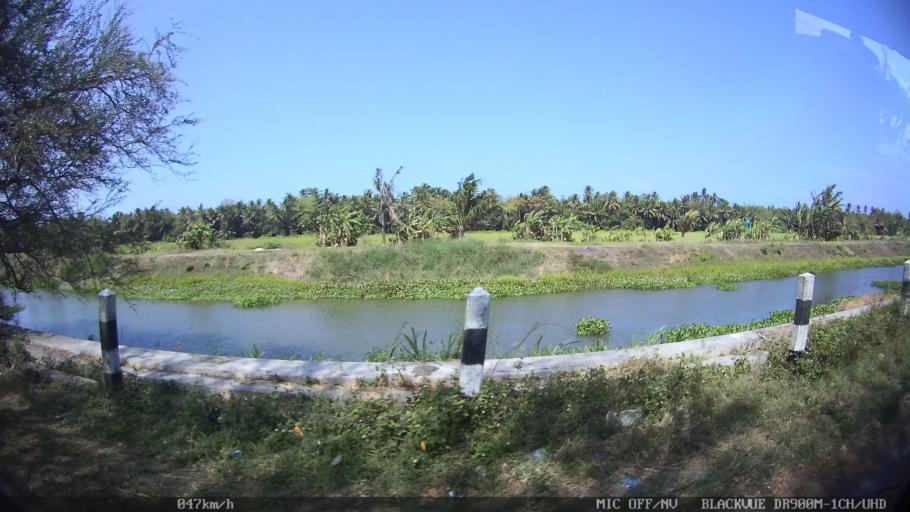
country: ID
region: Daerah Istimewa Yogyakarta
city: Srandakan
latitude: -7.9469
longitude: 110.1783
